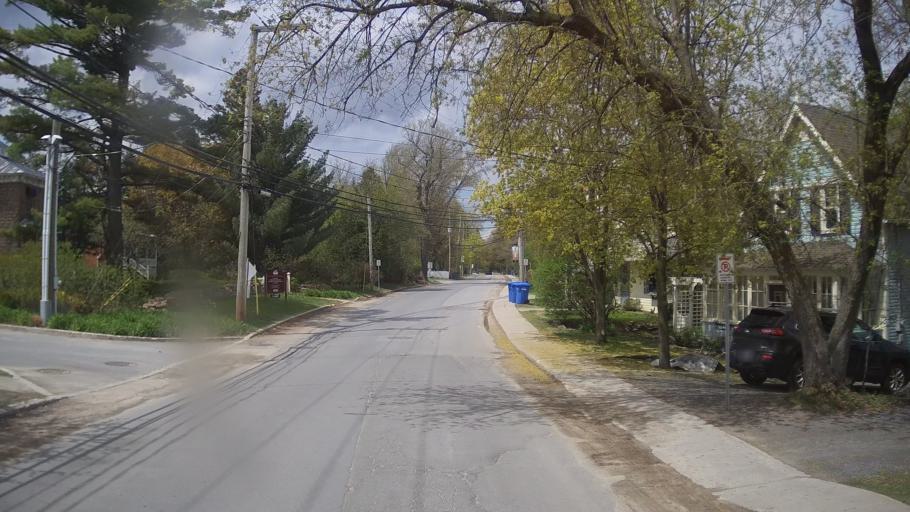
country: CA
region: Quebec
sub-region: Monteregie
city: Hudson
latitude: 45.4607
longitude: -74.1456
